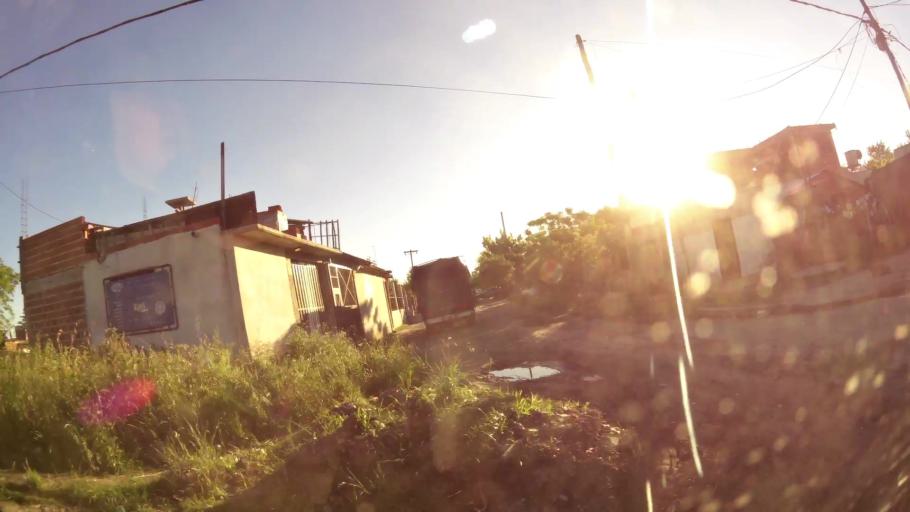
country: AR
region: Buenos Aires
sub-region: Partido de Almirante Brown
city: Adrogue
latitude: -34.7703
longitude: -58.3289
